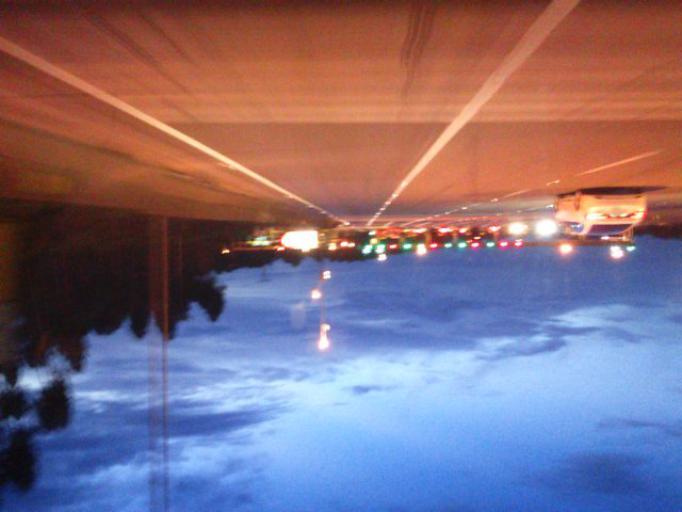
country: BR
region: Santa Catarina
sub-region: Barra Velha
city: Barra Velha
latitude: -26.5895
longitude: -48.7220
